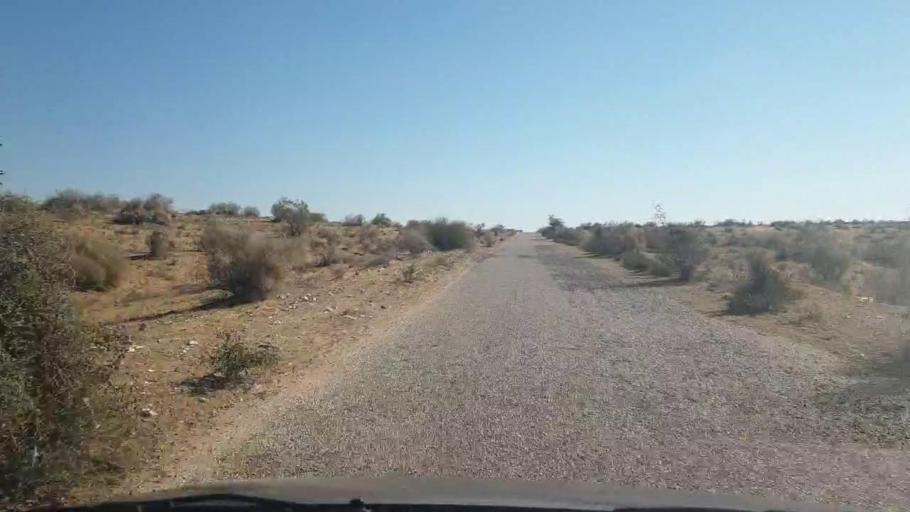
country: PK
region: Sindh
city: Bozdar
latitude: 27.0037
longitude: 68.8055
